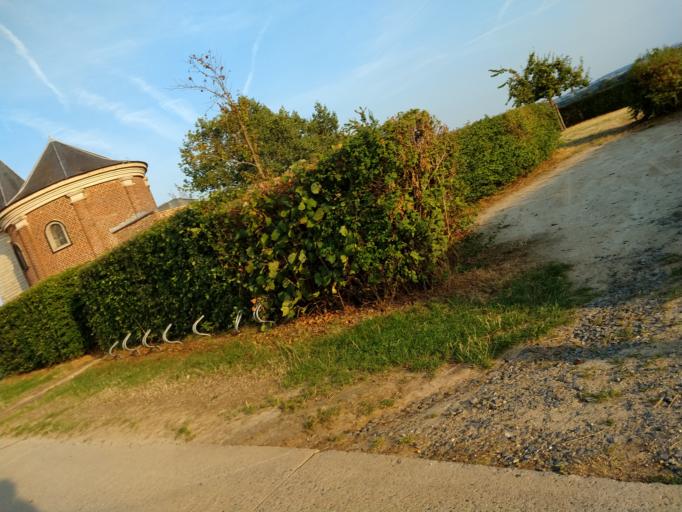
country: BE
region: Flanders
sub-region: Provincie Vlaams-Brabant
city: Hoegaarden
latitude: 50.7891
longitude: 4.8810
